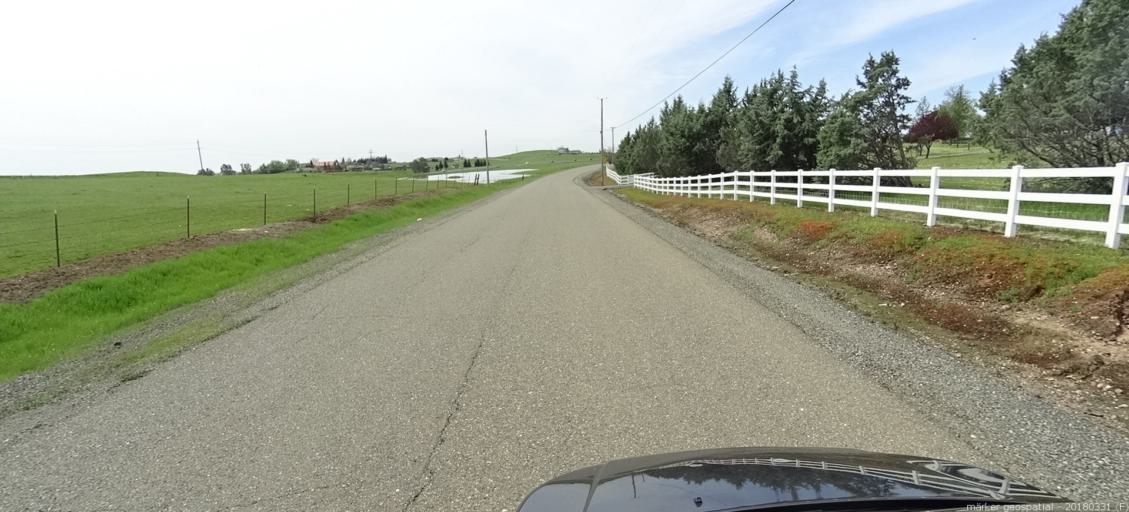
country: US
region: California
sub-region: Sacramento County
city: Rancho Murieta
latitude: 38.4982
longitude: -121.1259
